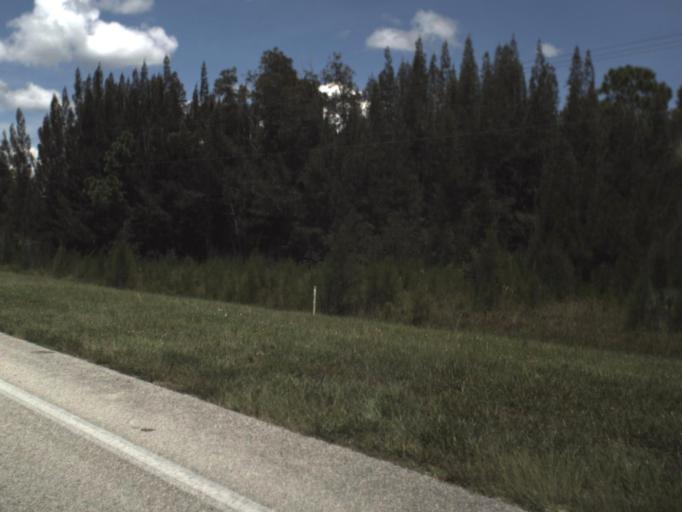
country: US
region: Florida
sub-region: Charlotte County
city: Charlotte Park
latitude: 26.8568
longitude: -81.9868
